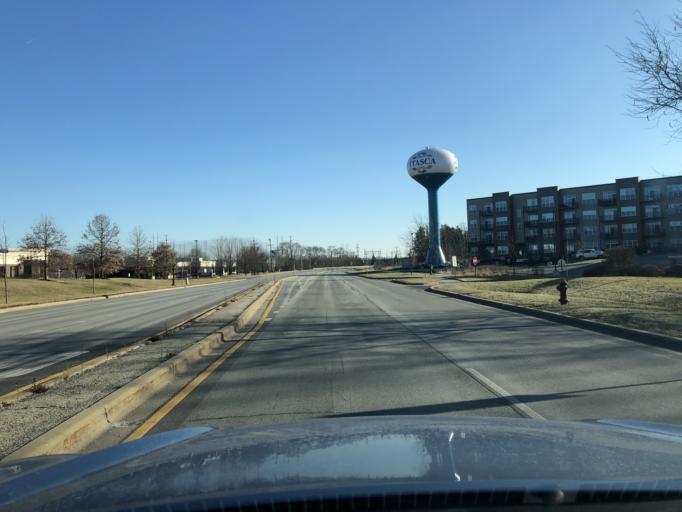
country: US
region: Illinois
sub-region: DuPage County
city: Itasca
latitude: 41.9878
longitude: -88.0018
